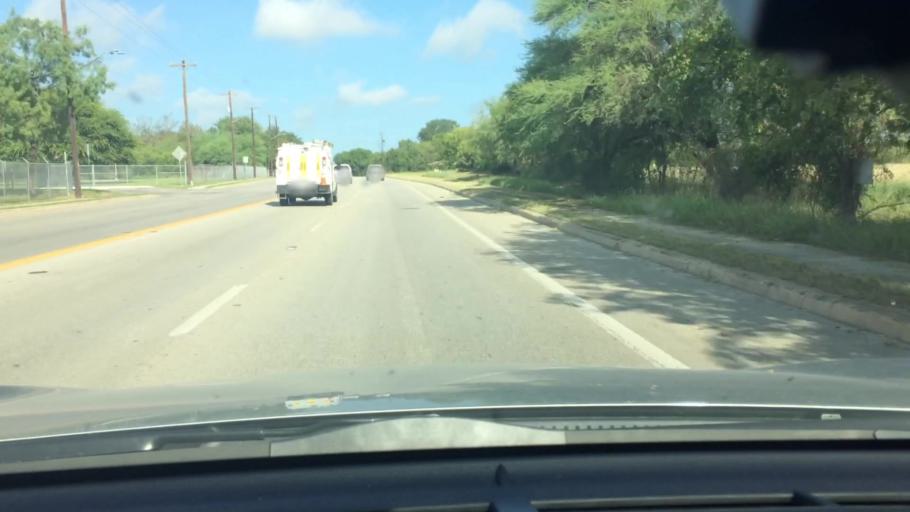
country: US
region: Texas
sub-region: Bexar County
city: China Grove
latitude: 29.3733
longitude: -98.3969
